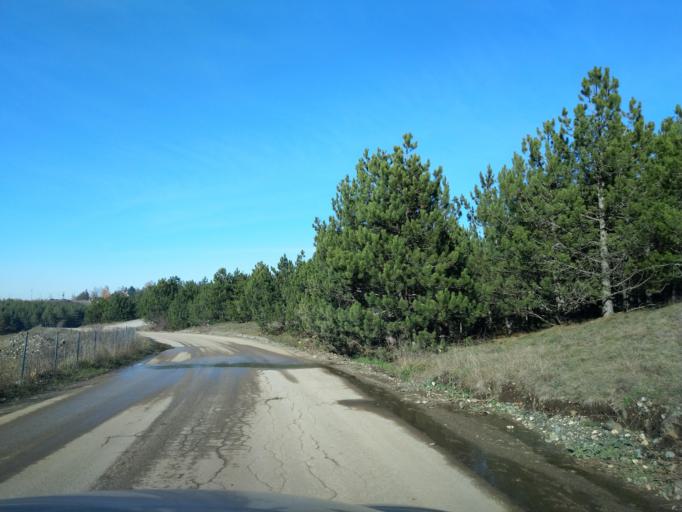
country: RS
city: Zlatibor
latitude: 43.7318
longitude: 19.6812
